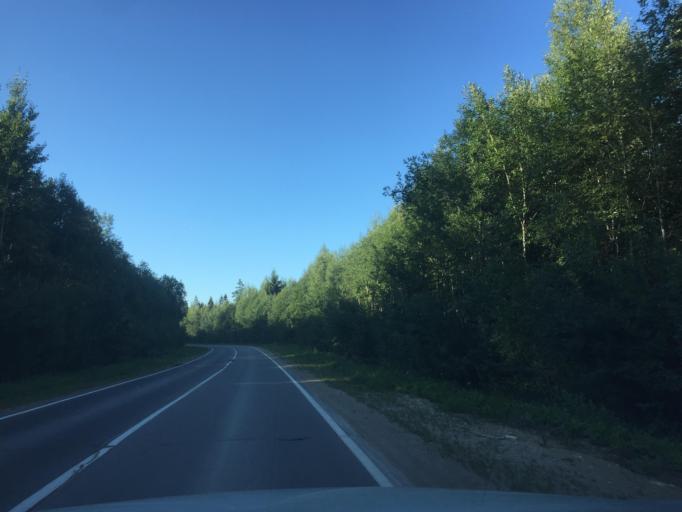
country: RU
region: Leningrad
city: Siverskiy
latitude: 59.3010
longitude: 30.0355
